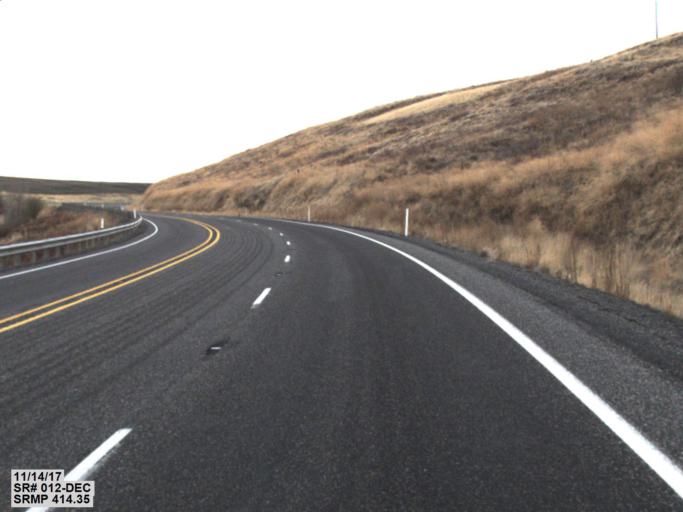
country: US
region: Washington
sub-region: Garfield County
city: Pomeroy
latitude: 46.4418
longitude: -117.4069
